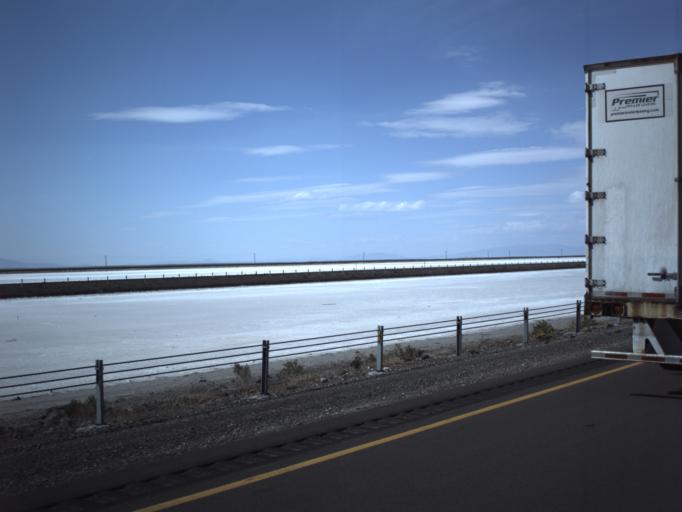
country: US
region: Utah
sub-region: Tooele County
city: Wendover
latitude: 40.7296
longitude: -113.4076
